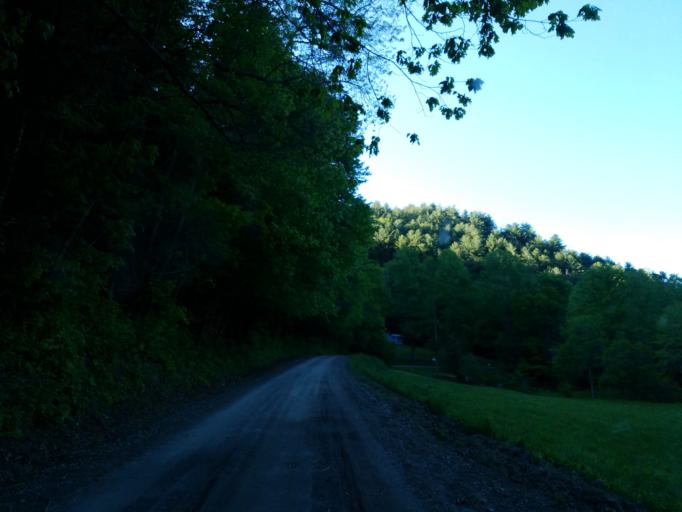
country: US
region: Georgia
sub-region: Fannin County
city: Blue Ridge
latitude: 34.7441
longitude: -84.2844
